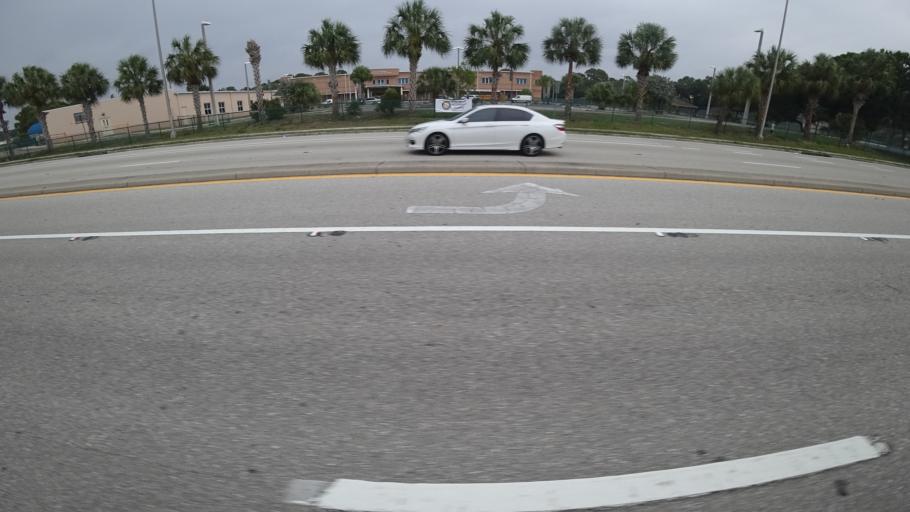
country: US
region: Florida
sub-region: Manatee County
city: Whitfield
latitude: 27.4292
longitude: -82.5567
